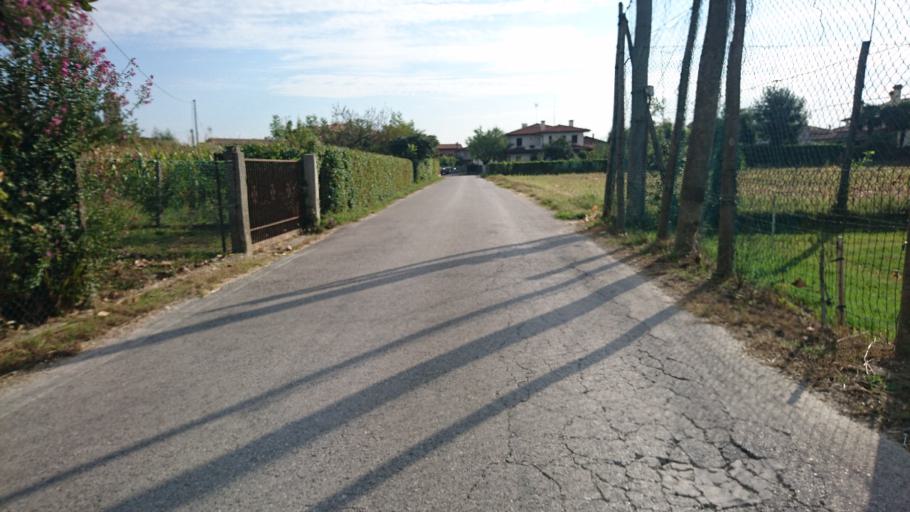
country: IT
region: Veneto
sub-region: Provincia di Venezia
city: Mira Taglio
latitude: 45.4232
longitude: 12.1504
